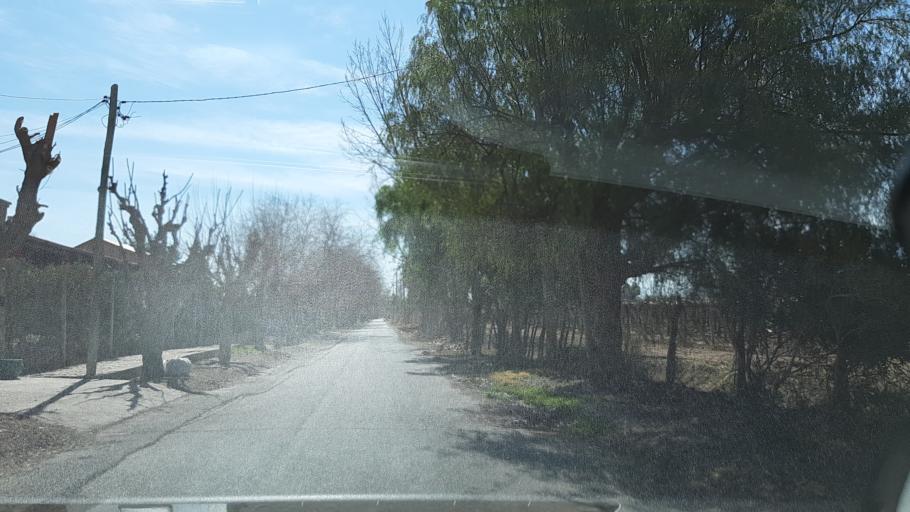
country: AR
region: San Juan
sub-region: Departamento de Zonda
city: Zonda
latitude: -31.5657
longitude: -68.7303
